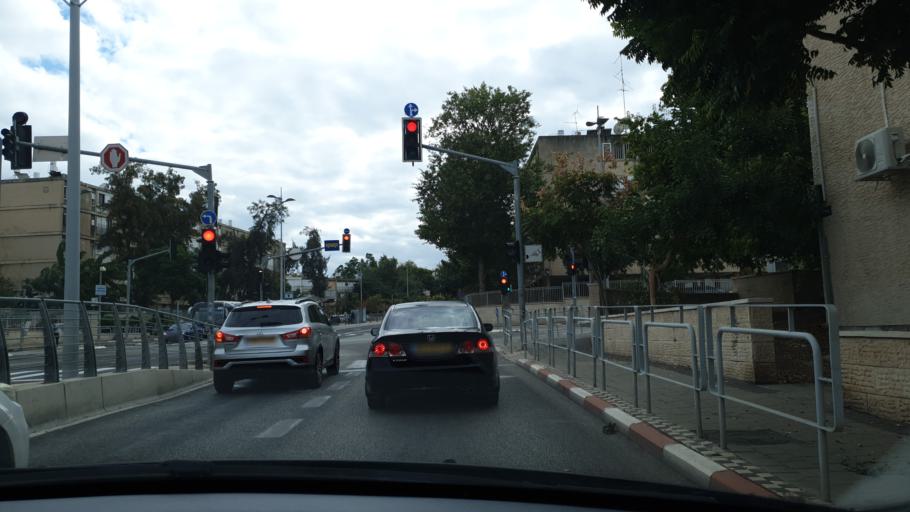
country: IL
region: Haifa
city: Qiryat Ata
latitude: 32.8138
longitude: 35.1140
